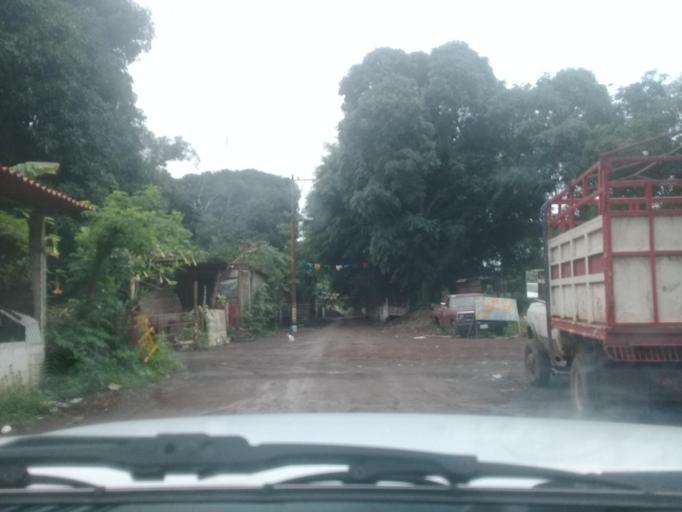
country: MX
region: Veracruz
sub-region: San Andres Tuxtla
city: Cerro las Iguanas
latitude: 18.4286
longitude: -95.1968
